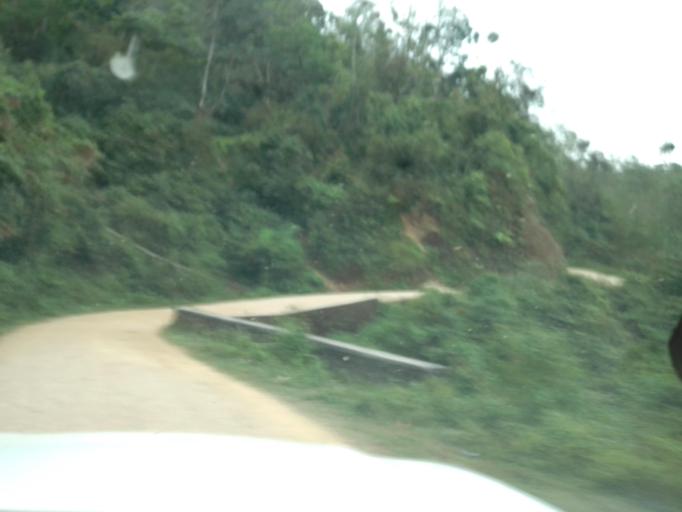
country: MX
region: Chiapas
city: Motozintla de Mendoza
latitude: 15.2212
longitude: -92.2253
